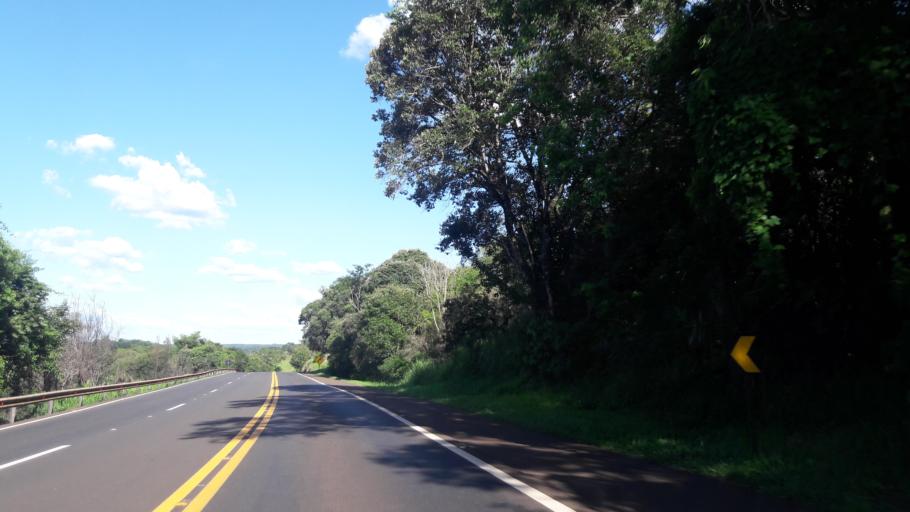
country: BR
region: Parana
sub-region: Laranjeiras Do Sul
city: Laranjeiras do Sul
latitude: -25.4053
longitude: -52.0969
